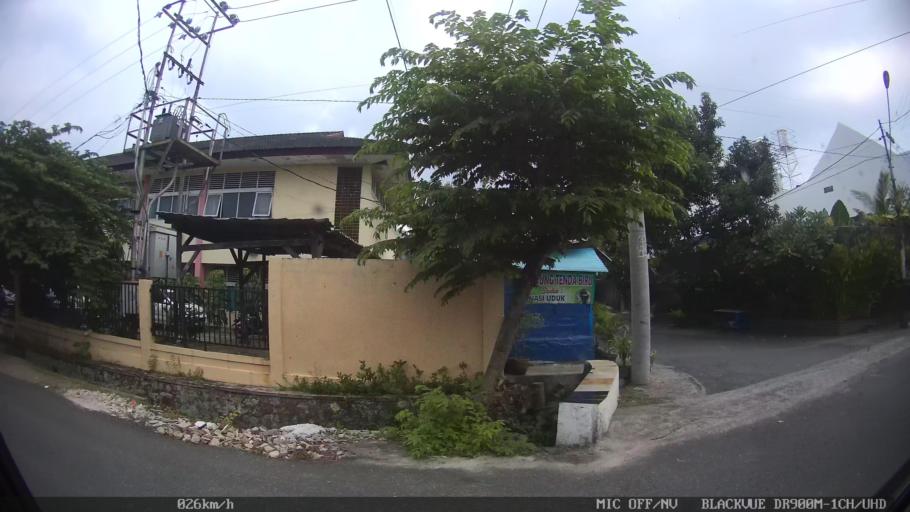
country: ID
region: Lampung
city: Bandarlampung
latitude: -5.4261
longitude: 105.2741
